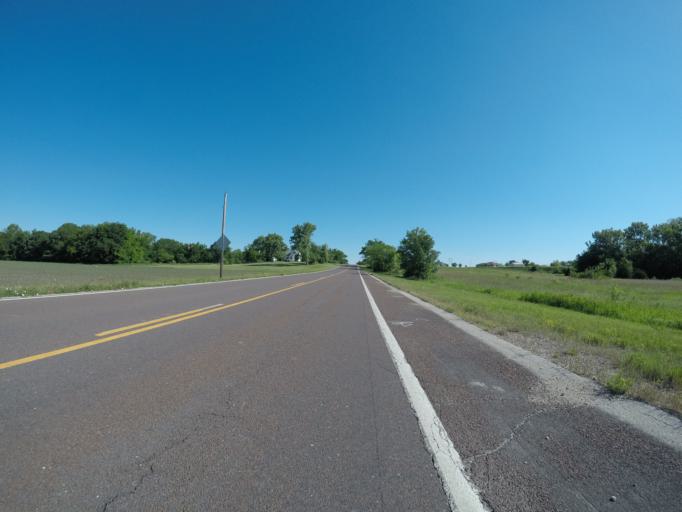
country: US
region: Kansas
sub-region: Lyon County
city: Emporia
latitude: 38.6562
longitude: -96.0975
